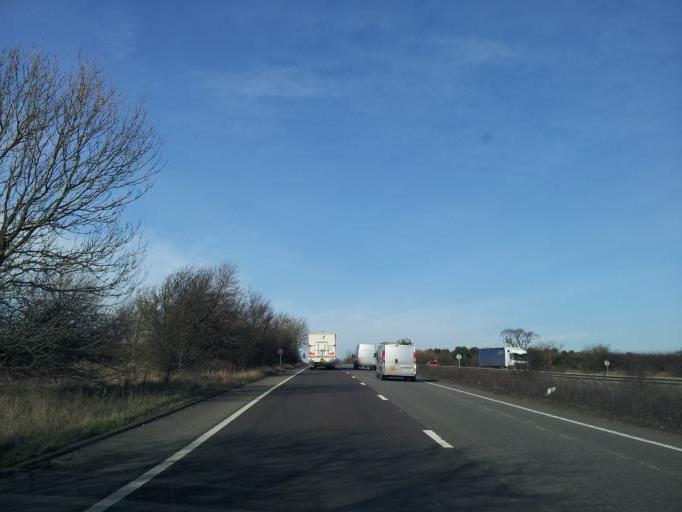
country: GB
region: England
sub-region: District of Rutland
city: Greetham
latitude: 52.7473
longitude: -0.6046
